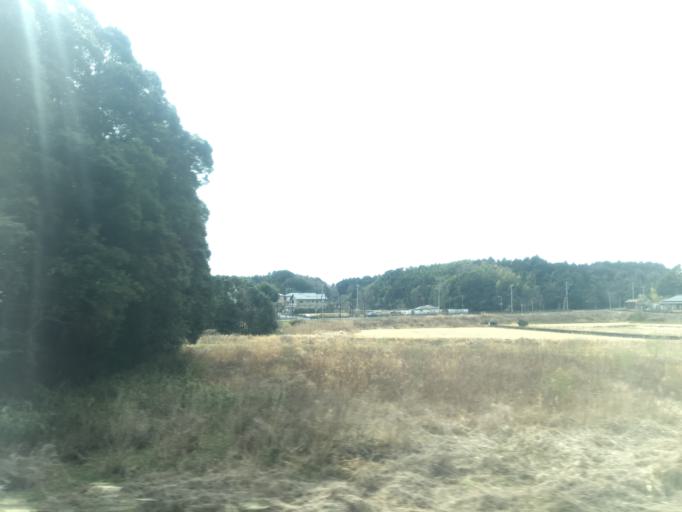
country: JP
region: Chiba
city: Narita
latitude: 35.7886
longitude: 140.3016
